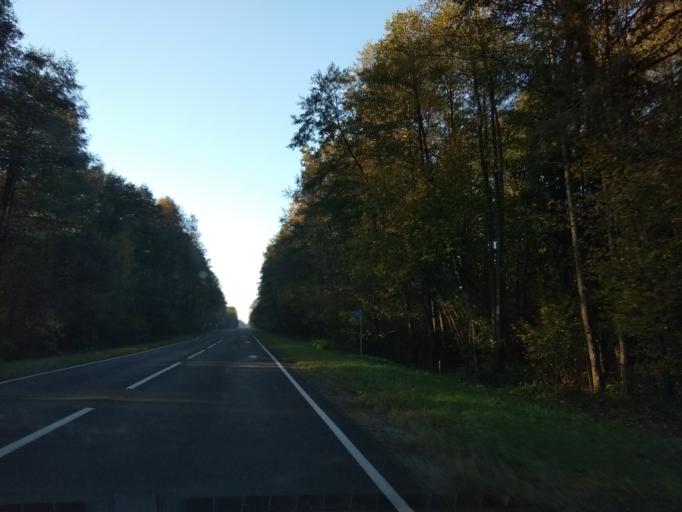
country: BY
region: Brest
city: Kobryn
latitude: 52.0640
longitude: 24.2837
